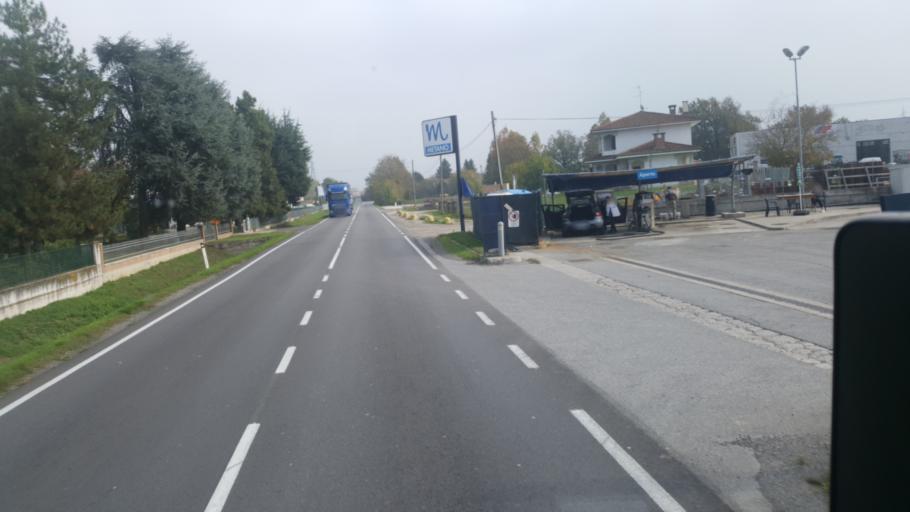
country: IT
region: Lombardy
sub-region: Provincia di Mantova
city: Pegognaga
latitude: 44.9872
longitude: 10.8398
